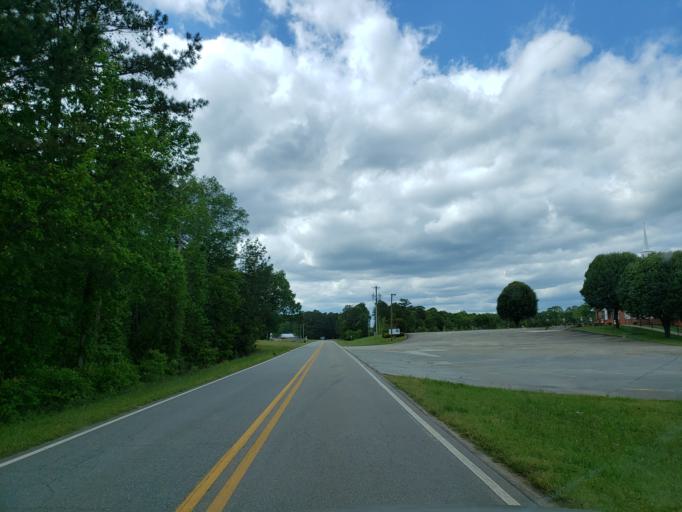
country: US
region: Georgia
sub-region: Haralson County
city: Tallapoosa
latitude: 33.7043
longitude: -85.3272
